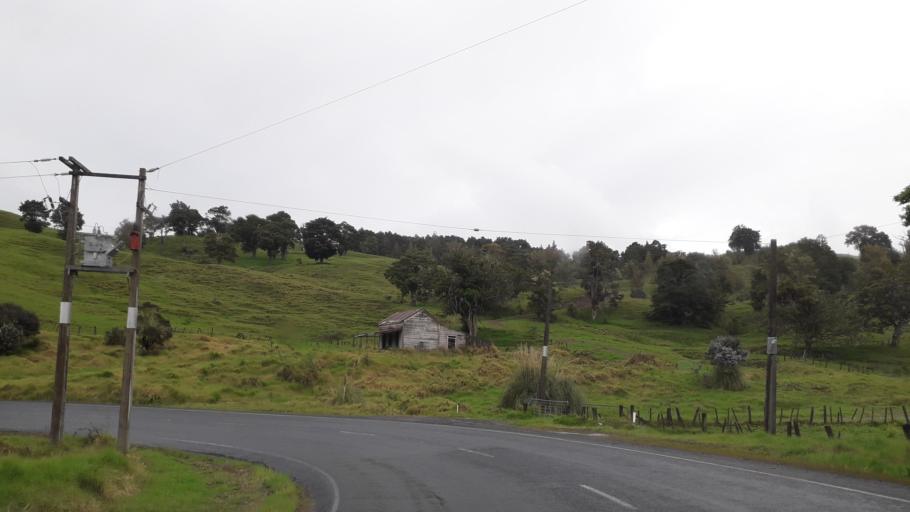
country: NZ
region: Northland
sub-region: Far North District
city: Kaitaia
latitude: -35.3602
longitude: 173.4944
